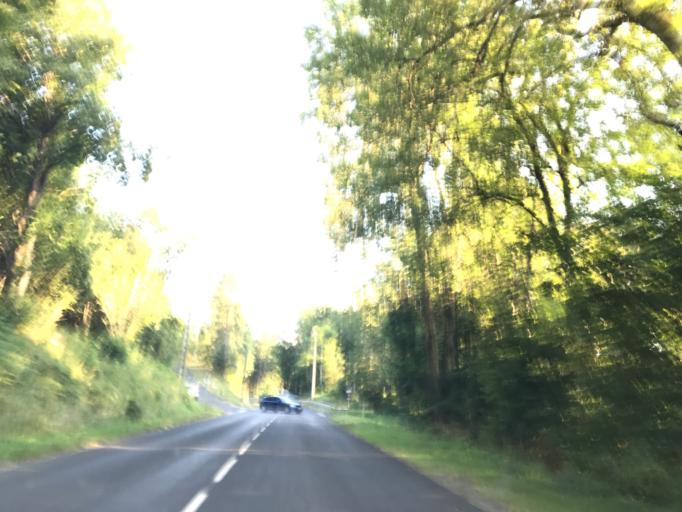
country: FR
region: Auvergne
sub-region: Departement du Puy-de-Dome
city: Saint-Remy-sur-Durolle
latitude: 45.8815
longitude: 3.5999
